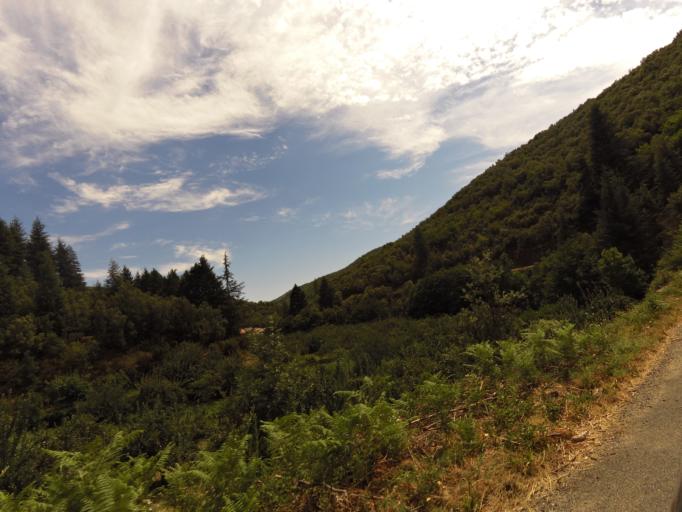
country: FR
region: Languedoc-Roussillon
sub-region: Departement du Gard
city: Le Vigan
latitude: 44.0137
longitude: 3.6454
